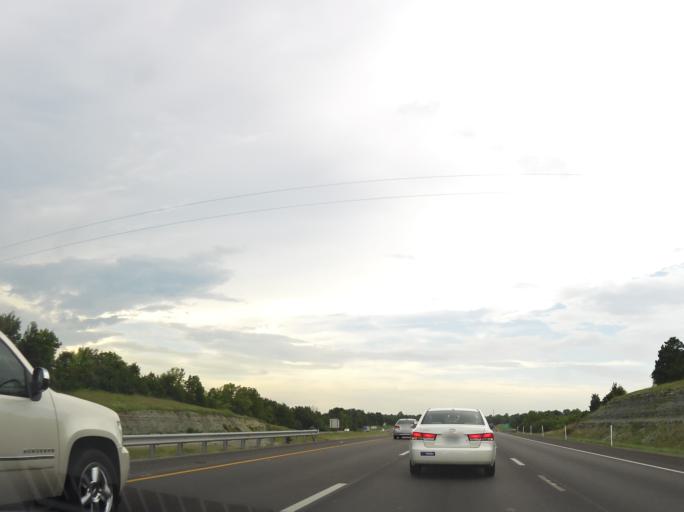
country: US
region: Kentucky
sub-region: Madison County
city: Richmond
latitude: 37.8055
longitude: -84.3243
